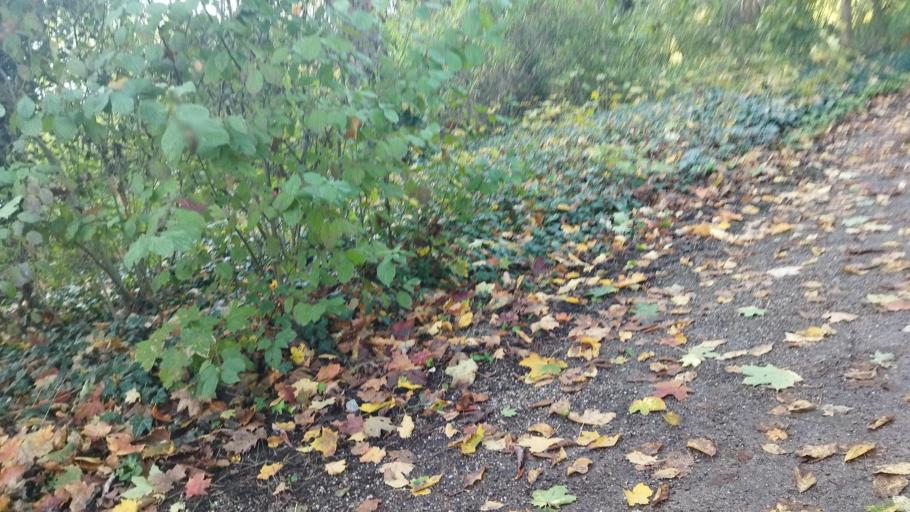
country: DE
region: Baden-Wuerttemberg
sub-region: Karlsruhe Region
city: Schwetzingen
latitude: 49.3803
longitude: 8.5644
